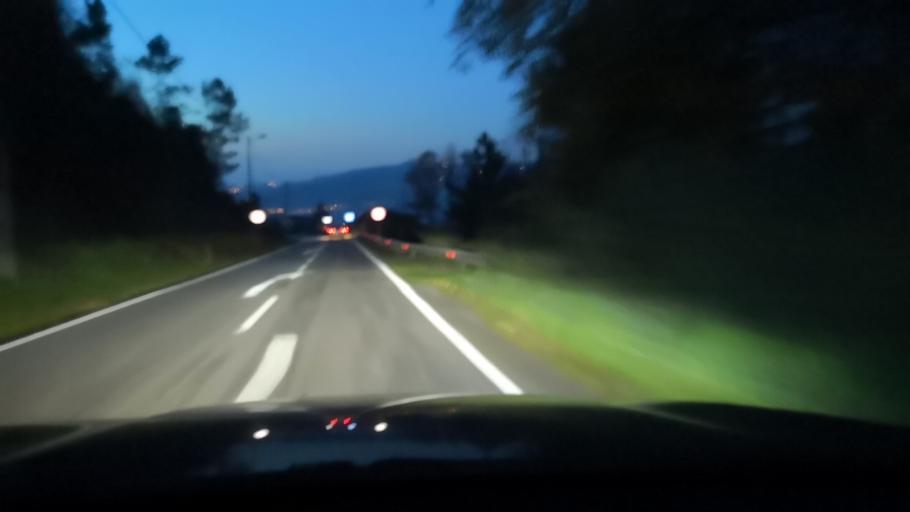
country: PT
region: Porto
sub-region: Amarante
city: Amarante
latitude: 41.2366
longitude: -8.0255
